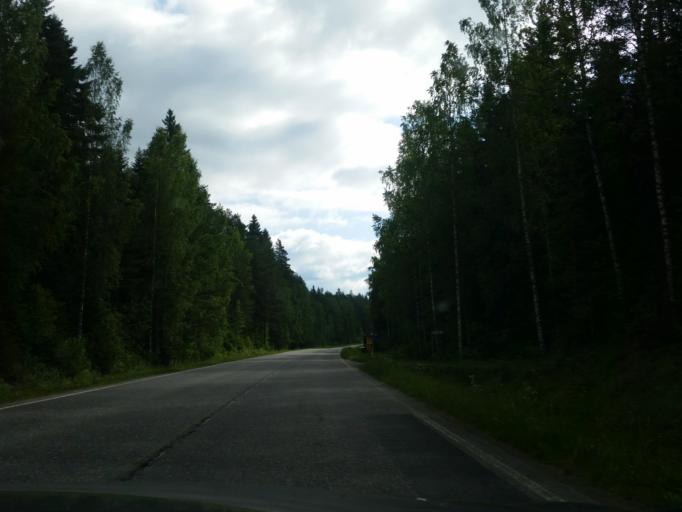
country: FI
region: Northern Savo
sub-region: Sisae-Savo
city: Tervo
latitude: 62.9582
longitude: 26.7710
